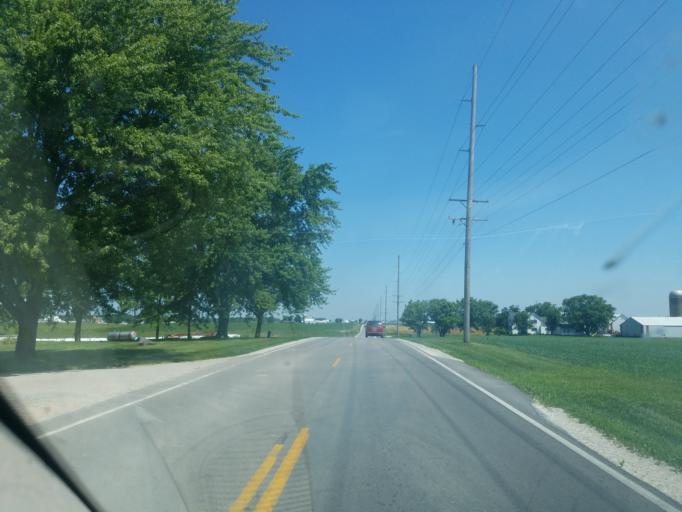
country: US
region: Ohio
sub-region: Mercer County
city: Saint Henry
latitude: 40.4405
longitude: -84.6482
